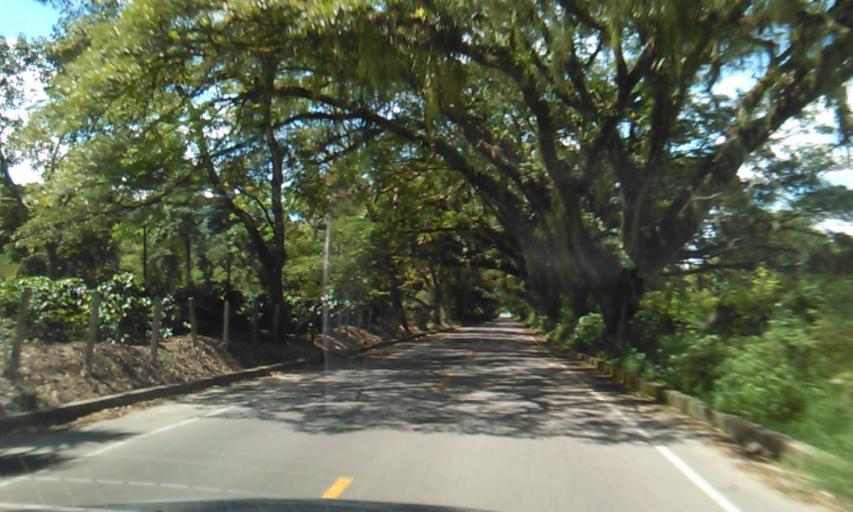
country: CO
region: Quindio
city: Cordoba
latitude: 4.4043
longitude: -75.7093
